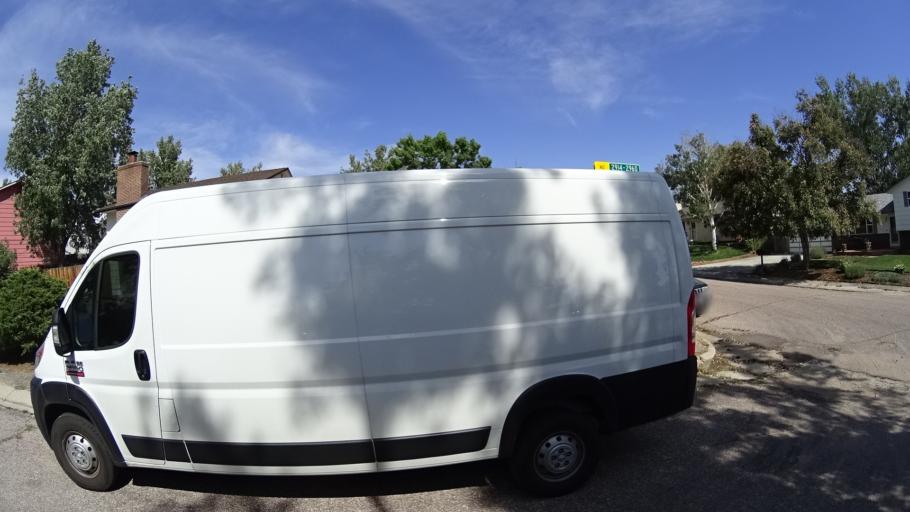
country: US
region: Colorado
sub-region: El Paso County
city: Cimarron Hills
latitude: 38.9100
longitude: -104.7723
